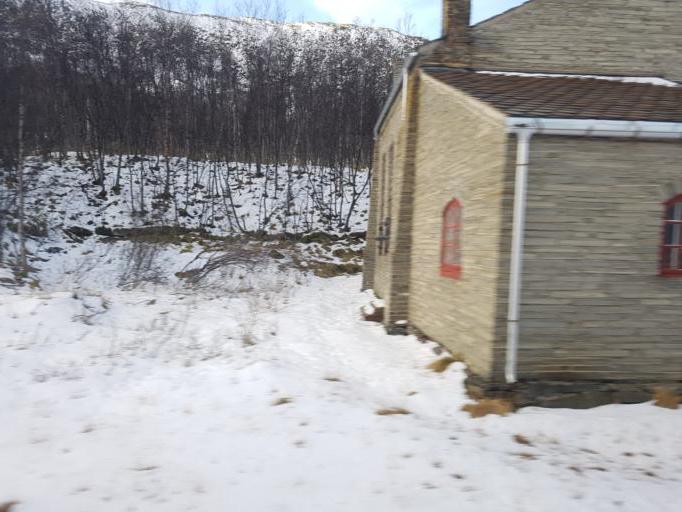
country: NO
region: Oppland
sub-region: Dovre
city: Dovre
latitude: 62.2182
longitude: 9.5465
